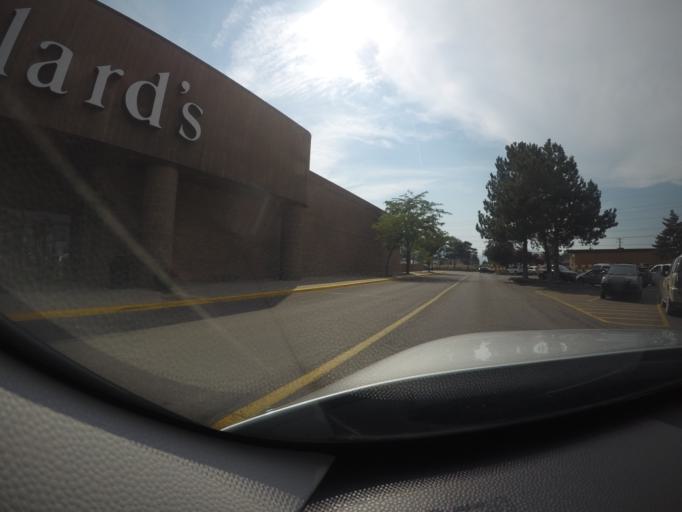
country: US
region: Montana
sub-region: Missoula County
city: Orchard Homes
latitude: 46.8478
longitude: -114.0274
